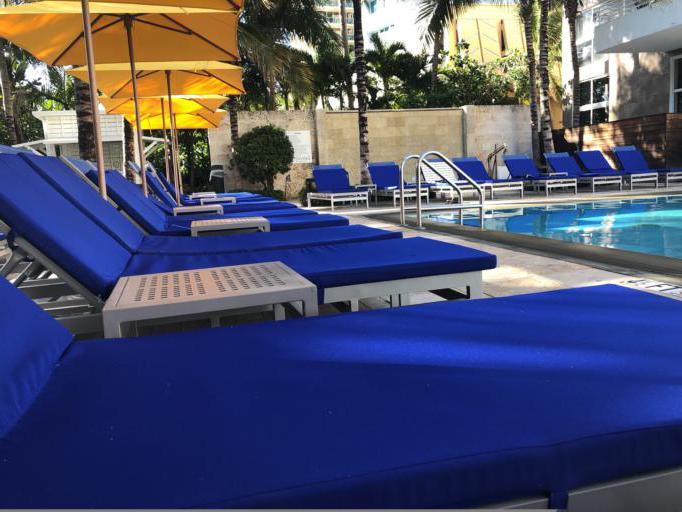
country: US
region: Florida
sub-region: Miami-Dade County
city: Miami Beach
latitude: 25.7885
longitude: -80.1285
